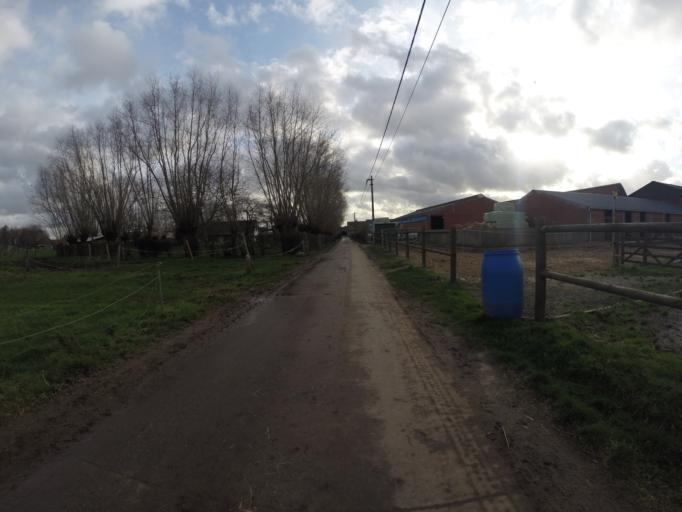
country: BE
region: Flanders
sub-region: Provincie Oost-Vlaanderen
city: Knesselare
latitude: 51.1176
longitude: 3.4115
